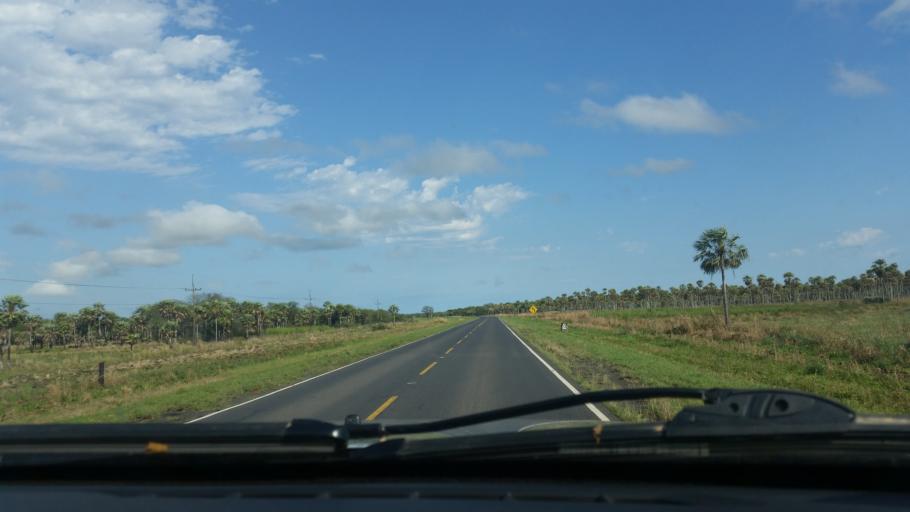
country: PY
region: Presidente Hayes
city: Benjamin Aceval
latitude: -24.9113
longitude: -57.6282
